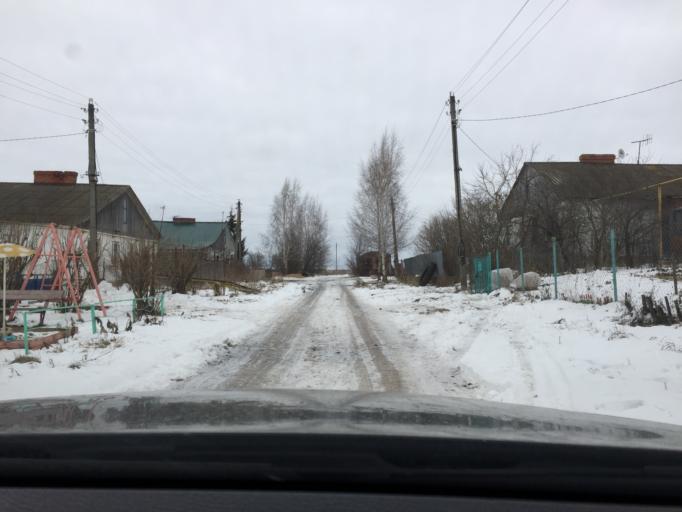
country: RU
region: Tula
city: Priupskiy
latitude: 53.7782
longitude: 37.6530
